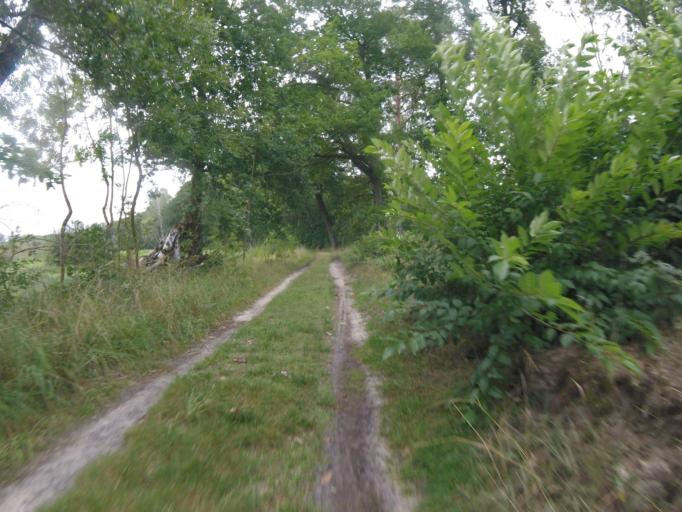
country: DE
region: Brandenburg
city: Bestensee
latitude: 52.2175
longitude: 13.6480
